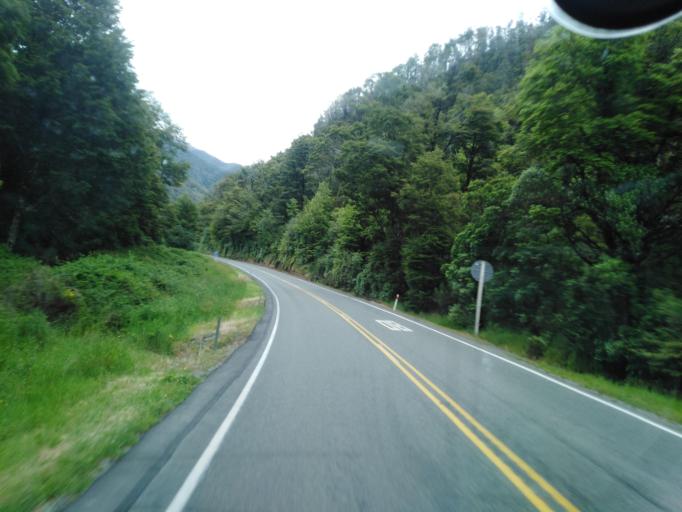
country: NZ
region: Tasman
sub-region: Tasman District
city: Wakefield
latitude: -41.7105
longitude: 172.5611
